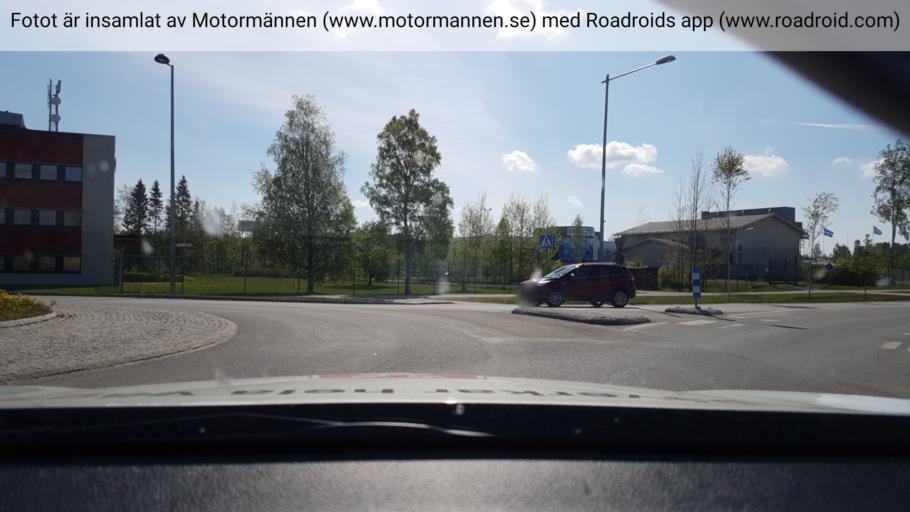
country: SE
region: Vaesterbotten
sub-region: Umea Kommun
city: Ersmark
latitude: 63.8507
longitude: 20.3146
